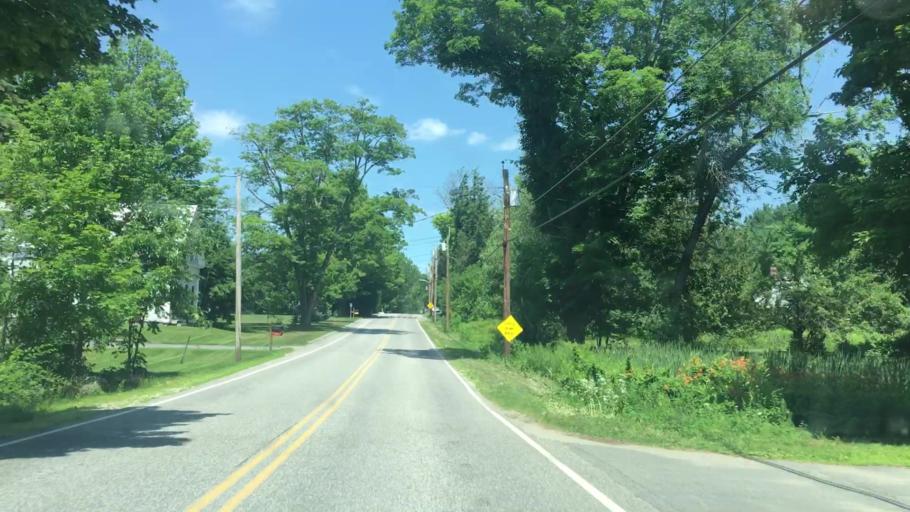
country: US
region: Maine
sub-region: Kennebec County
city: Wayne
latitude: 44.3457
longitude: -70.0643
